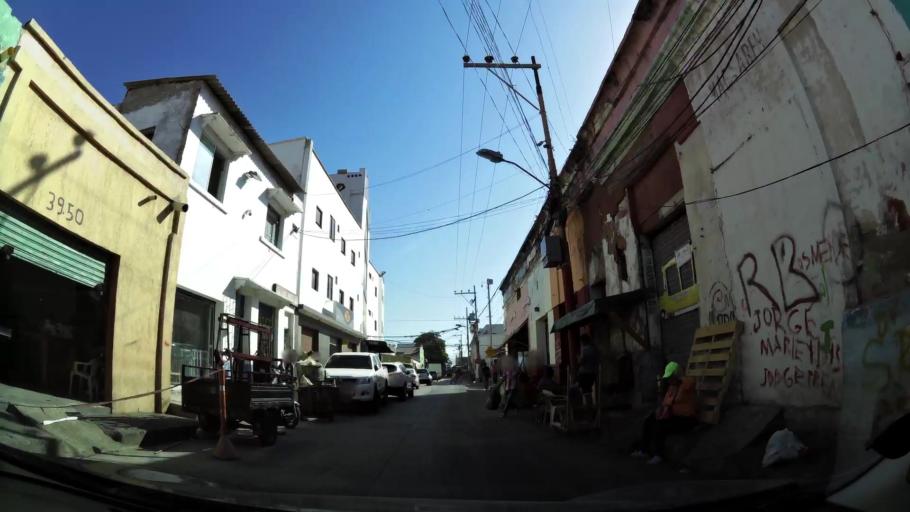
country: CO
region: Atlantico
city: Barranquilla
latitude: 10.9783
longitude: -74.7783
